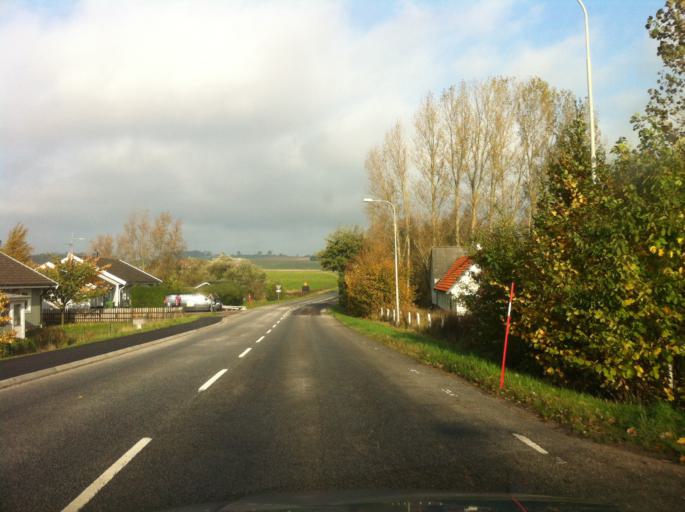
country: SE
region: Skane
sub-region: Landskrona
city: Asmundtorp
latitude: 55.8859
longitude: 12.9430
